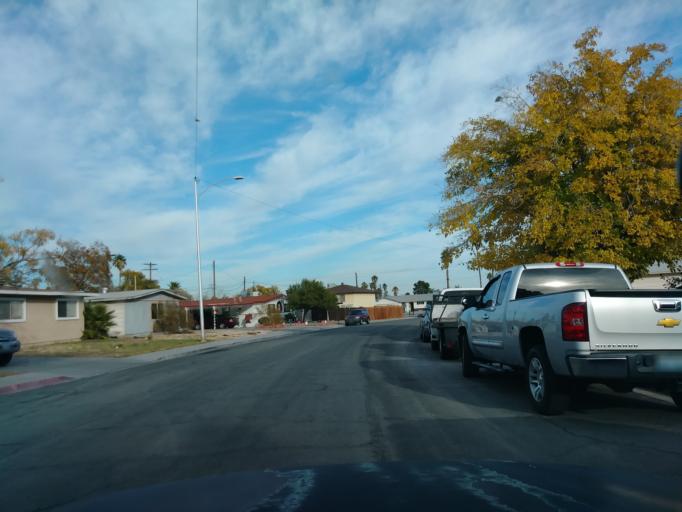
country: US
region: Nevada
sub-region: Clark County
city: Spring Valley
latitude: 36.1696
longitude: -115.2274
